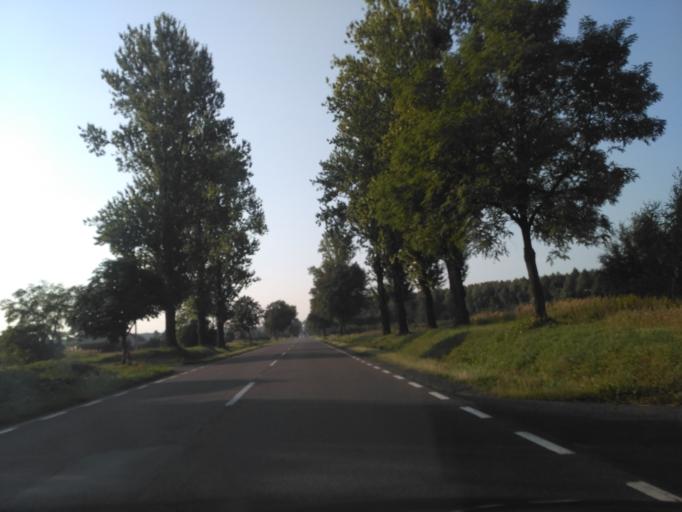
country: PL
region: Lublin Voivodeship
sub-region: Powiat krasnicki
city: Krasnik
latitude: 50.8759
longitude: 22.2664
